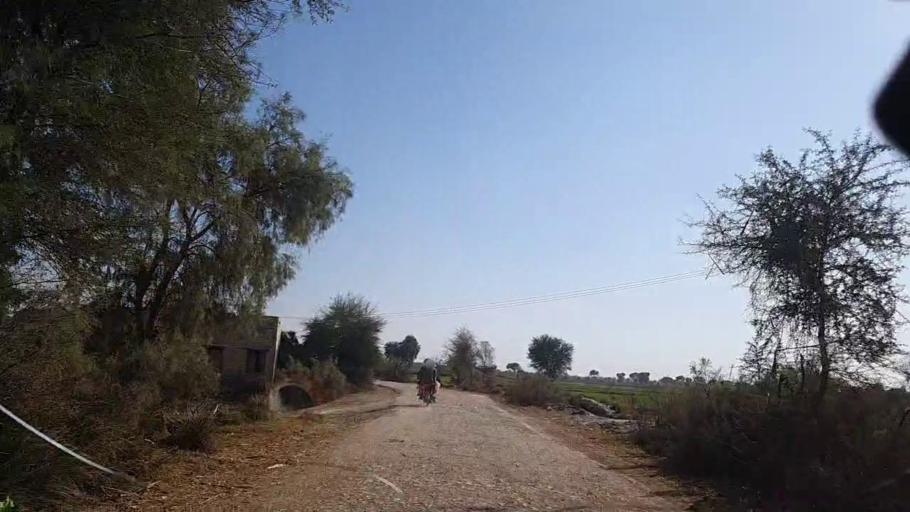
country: PK
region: Sindh
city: Khanpur
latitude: 27.8048
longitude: 69.3699
